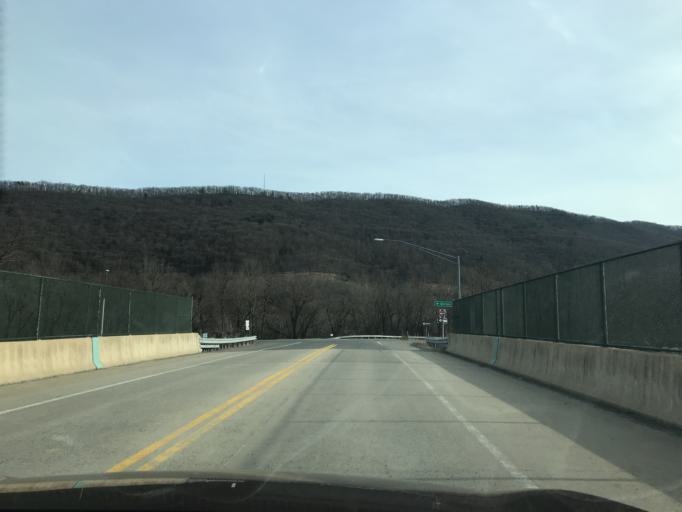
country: US
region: Pennsylvania
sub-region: Lycoming County
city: Duboistown
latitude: 41.2237
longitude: -77.0618
